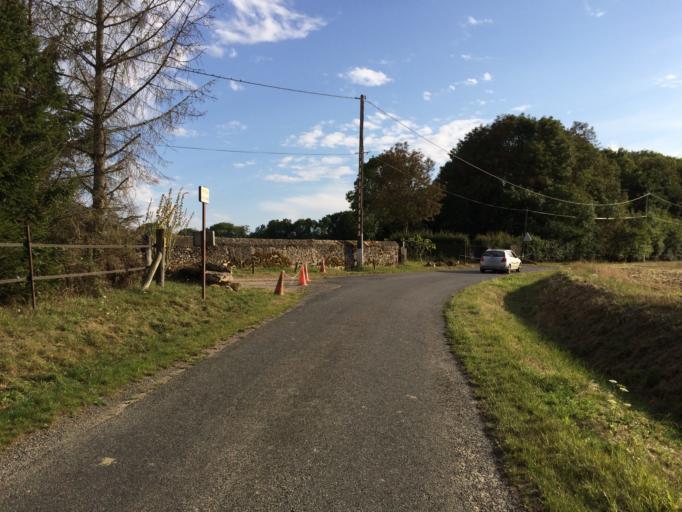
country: FR
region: Ile-de-France
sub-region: Departement de l'Essonne
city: Les Ulis
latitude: 48.6645
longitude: 2.1793
